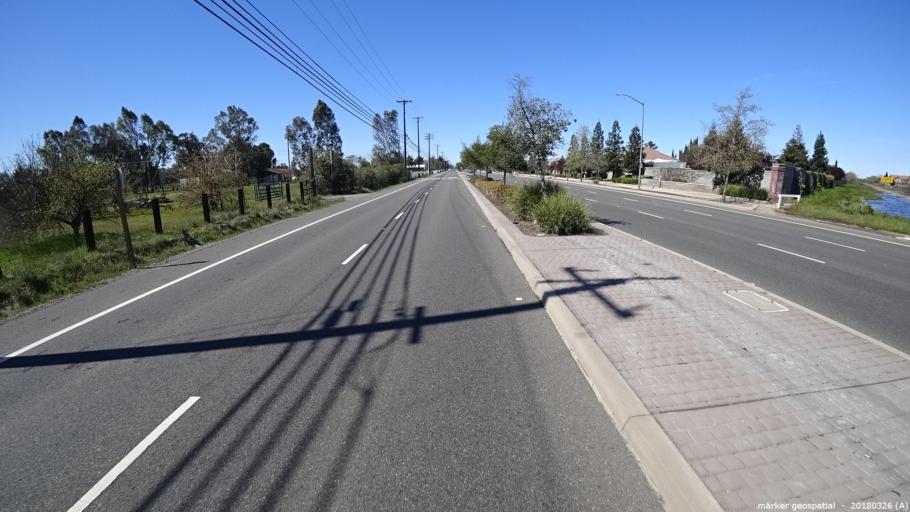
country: US
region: California
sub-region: Sacramento County
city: Vineyard
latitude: 38.4526
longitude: -121.3186
